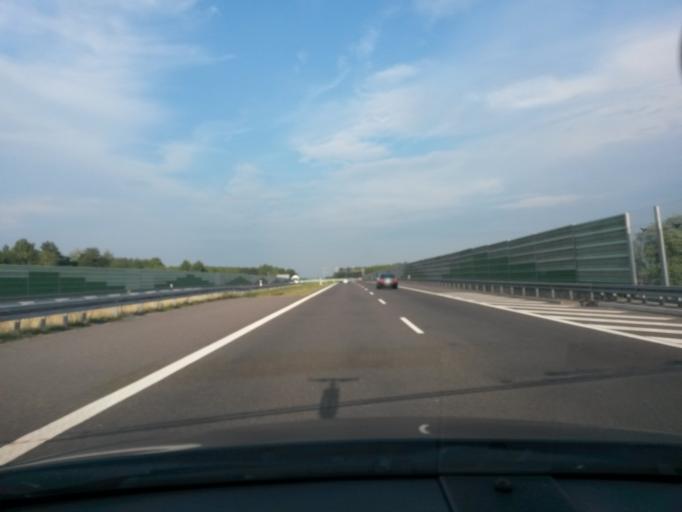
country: PL
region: Lodz Voivodeship
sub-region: Powiat zgierski
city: Zgierz
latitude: 51.9213
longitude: 19.3614
